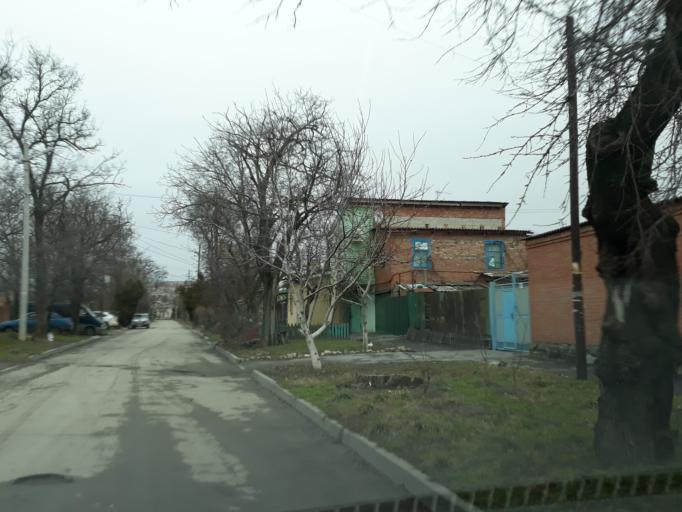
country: RU
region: Rostov
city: Taganrog
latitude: 47.2029
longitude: 38.9289
